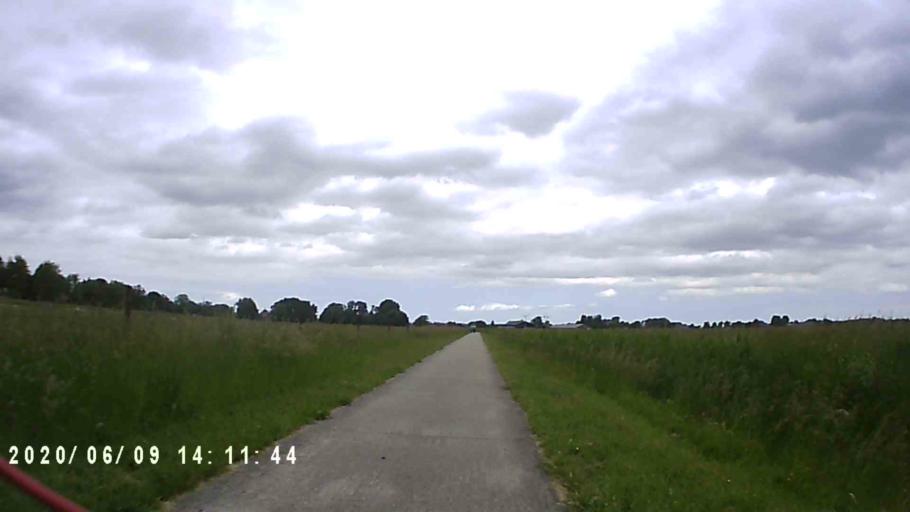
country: NL
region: Groningen
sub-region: Gemeente Bedum
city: Bedum
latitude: 53.2718
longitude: 6.6039
